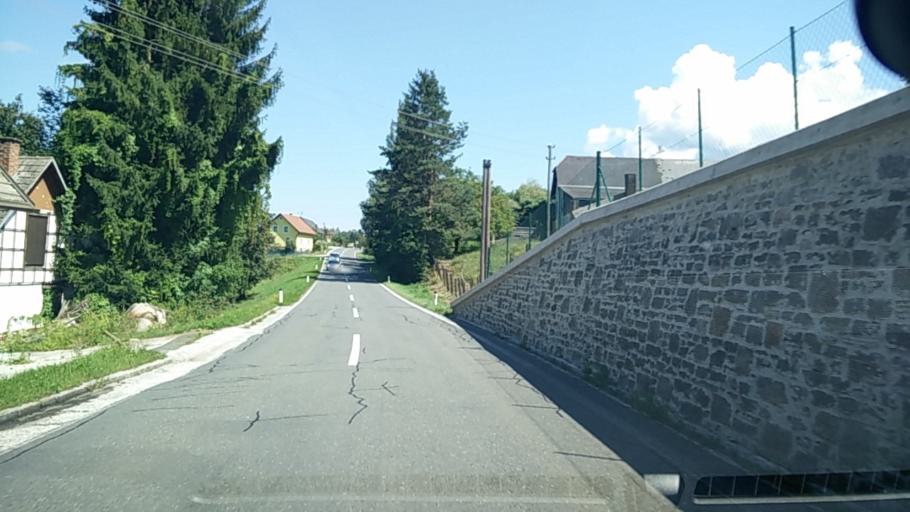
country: AT
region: Carinthia
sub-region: Politischer Bezirk Volkermarkt
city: Gallizien
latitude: 46.5396
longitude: 14.5564
